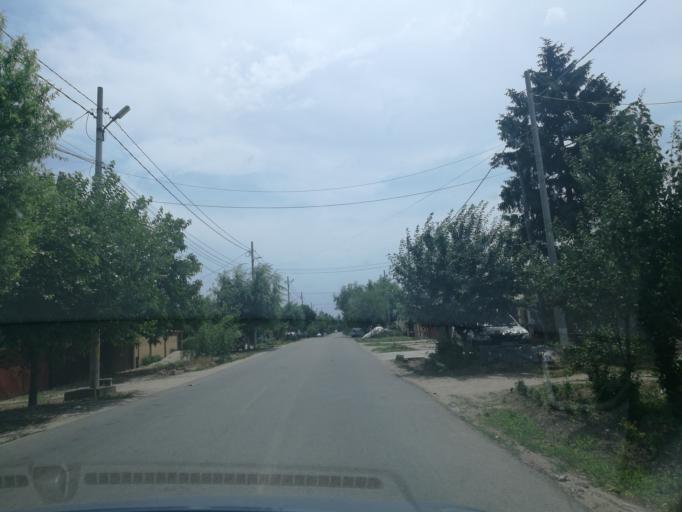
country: RO
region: Ilfov
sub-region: Comuna Vidra
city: Sintesti
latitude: 44.3089
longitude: 26.1141
